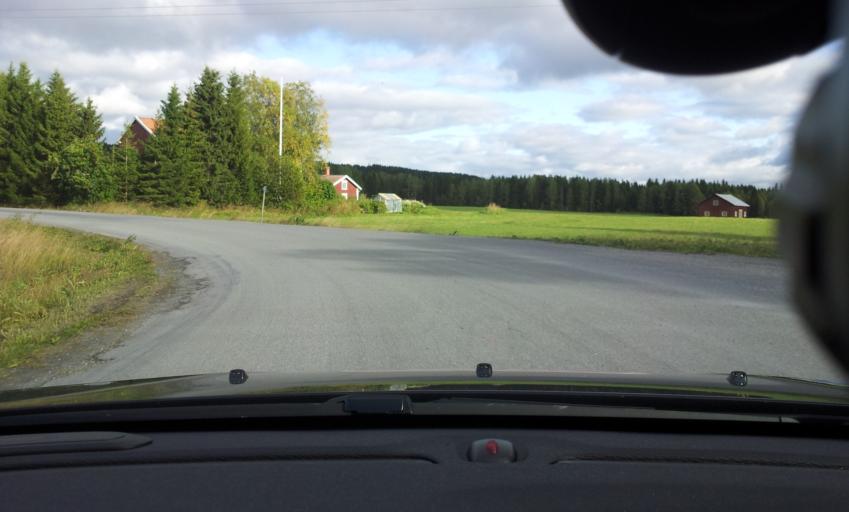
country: SE
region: Jaemtland
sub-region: OEstersunds Kommun
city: Brunflo
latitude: 63.0908
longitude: 14.8203
